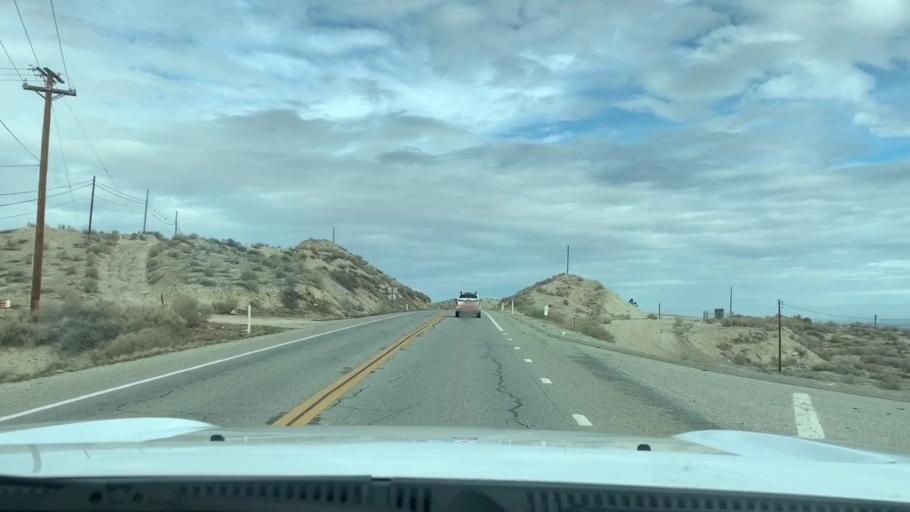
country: US
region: California
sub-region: Kern County
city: Maricopa
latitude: 35.0772
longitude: -119.4016
